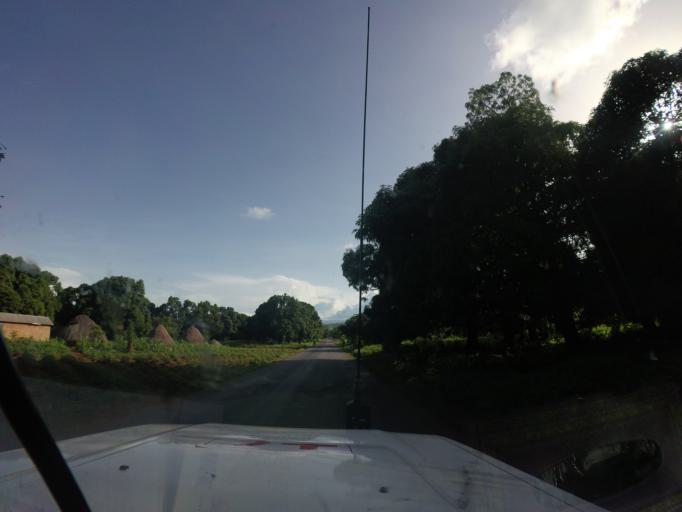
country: GN
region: Kindia
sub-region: Kindia
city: Kindia
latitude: 10.0197
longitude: -12.6802
